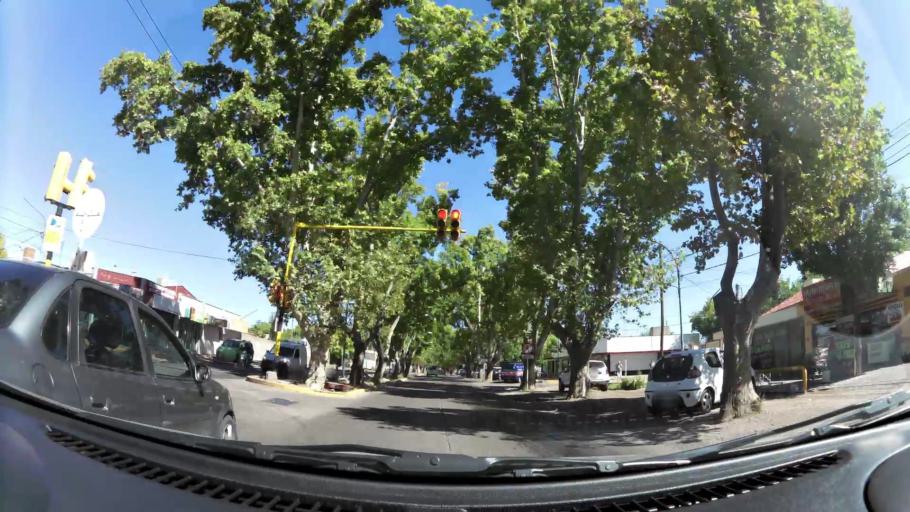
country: AR
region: Mendoza
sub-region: Departamento de Godoy Cruz
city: Godoy Cruz
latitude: -32.9402
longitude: -68.8324
